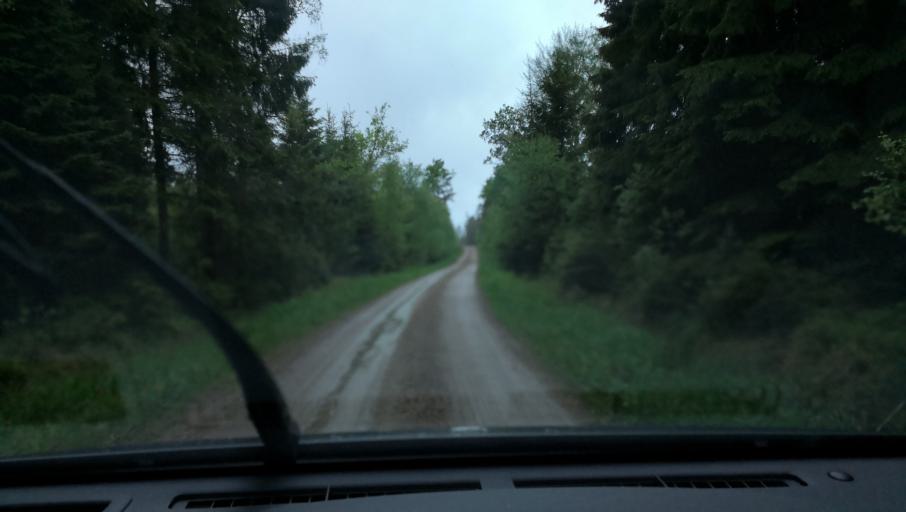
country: SE
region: Uppsala
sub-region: Enkopings Kommun
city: Orsundsbro
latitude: 59.9275
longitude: 17.3322
